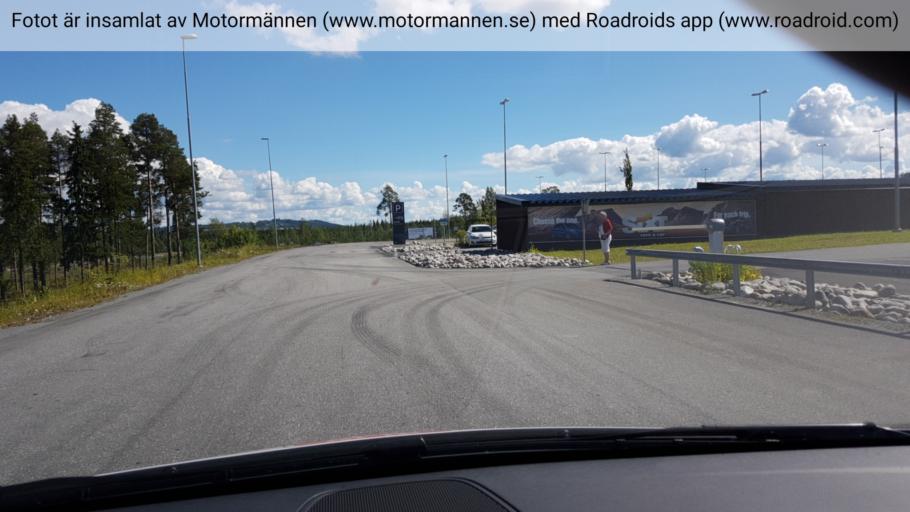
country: SE
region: Jaemtland
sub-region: Krokoms Kommun
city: Krokom
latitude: 63.1993
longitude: 14.4982
